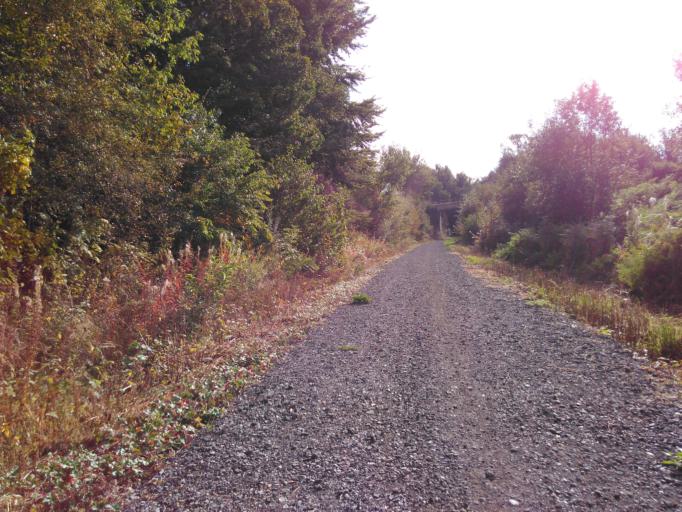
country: BE
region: Wallonia
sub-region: Province du Luxembourg
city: Neufchateau
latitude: 49.9188
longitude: 5.4173
